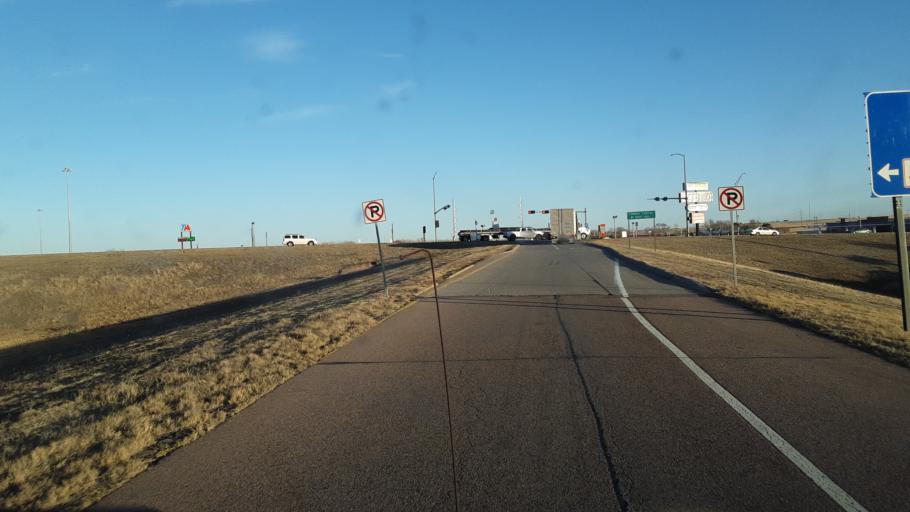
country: US
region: Nebraska
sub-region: Keith County
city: Ogallala
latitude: 41.1142
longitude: -101.7168
